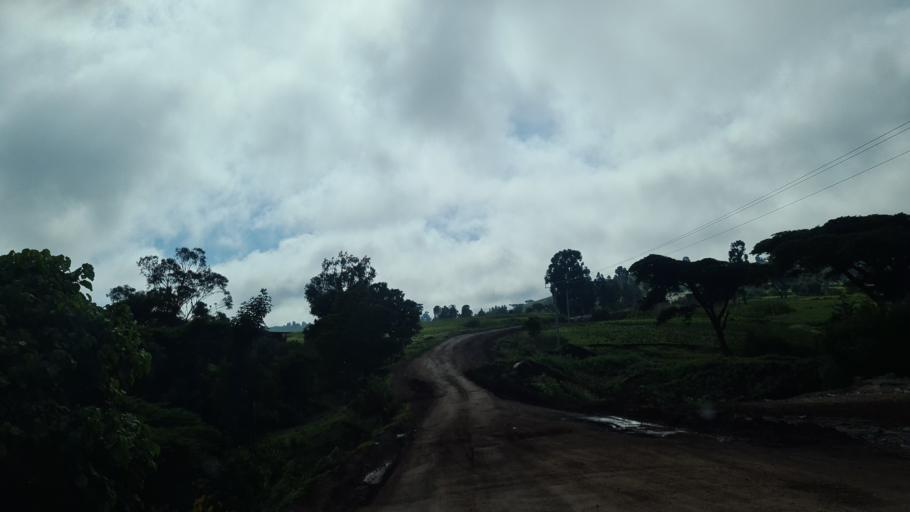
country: ET
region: Oromiya
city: Huruta
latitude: 8.1306
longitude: 39.3849
